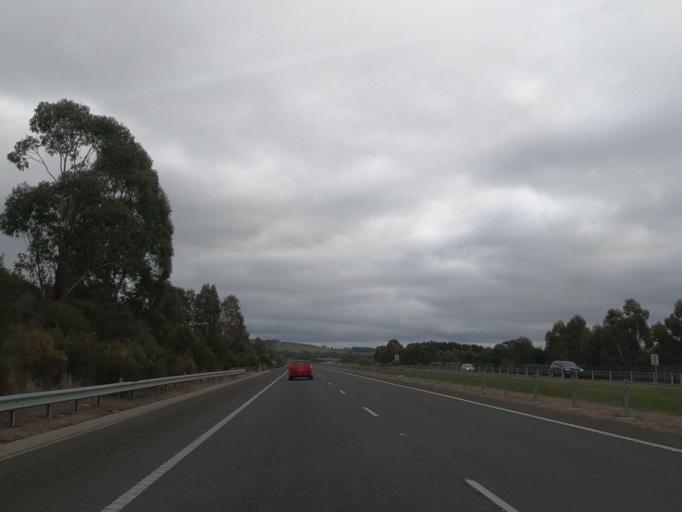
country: AU
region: Victoria
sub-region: Mount Alexander
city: Castlemaine
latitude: -37.0944
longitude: 144.3435
